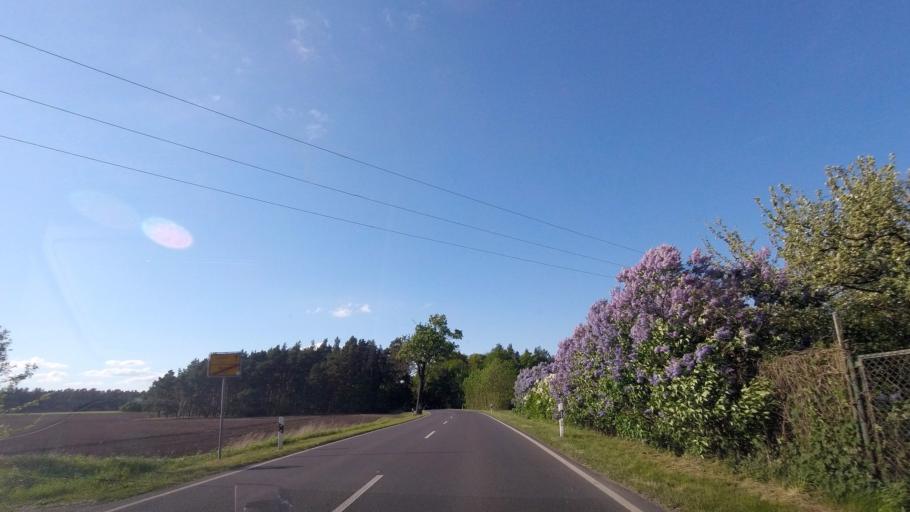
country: DE
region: Brandenburg
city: Luebben
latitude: 51.8905
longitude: 13.9005
